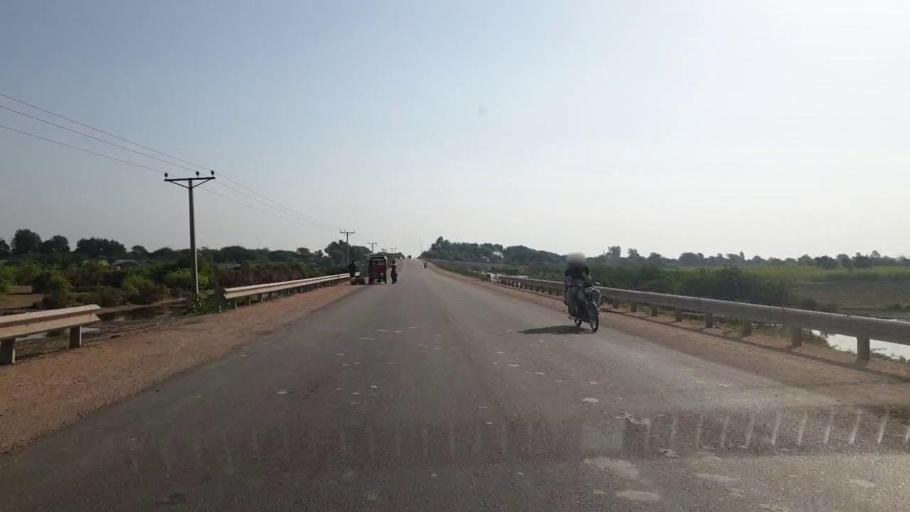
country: PK
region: Sindh
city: Tando Bago
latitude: 24.6579
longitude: 68.9753
